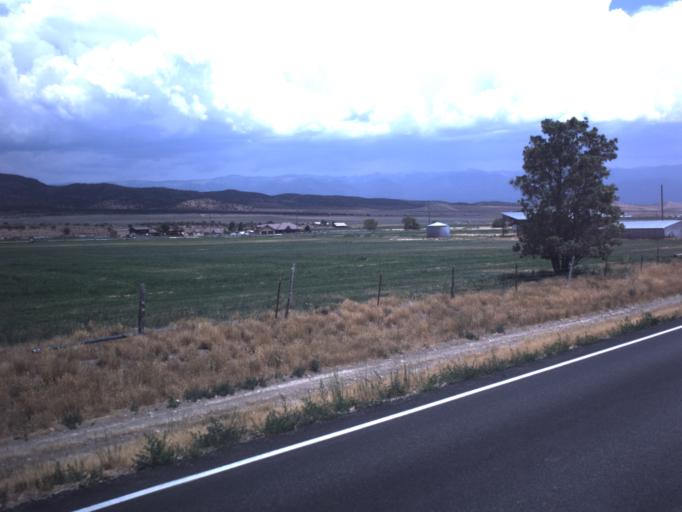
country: US
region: Utah
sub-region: Sanpete County
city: Fountain Green
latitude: 39.6124
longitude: -111.6276
